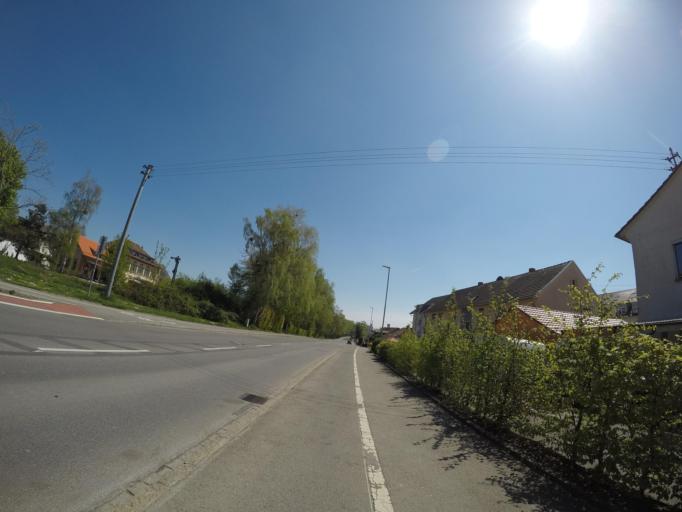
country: DE
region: Baden-Wuerttemberg
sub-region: Tuebingen Region
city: Markdorf
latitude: 47.7168
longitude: 9.3876
